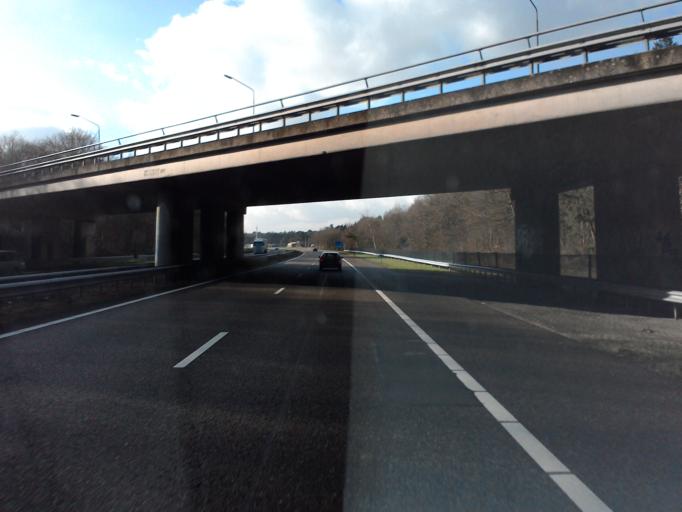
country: NL
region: North Brabant
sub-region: Gemeente Veldhoven
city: Veldhoven
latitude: 51.3965
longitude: 5.3901
